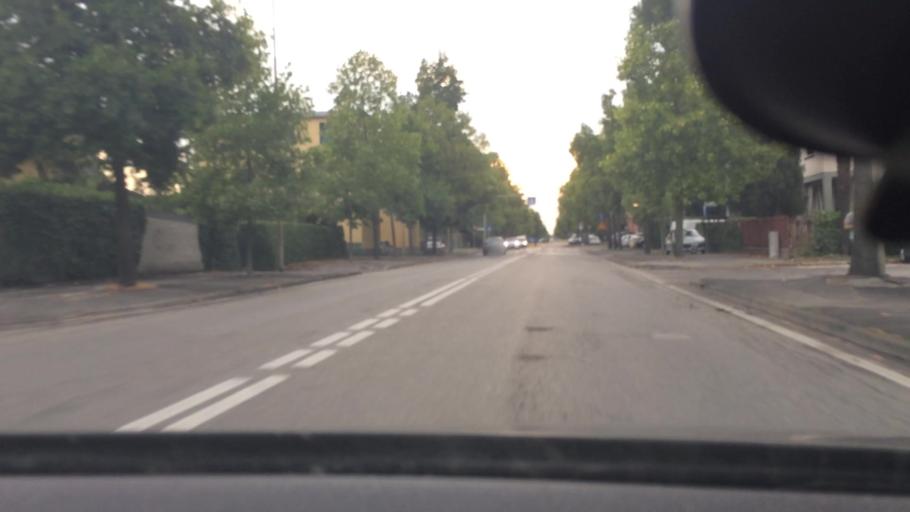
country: IT
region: Lombardy
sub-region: Provincia di Monza e Brianza
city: Nova Milanese
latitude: 45.5925
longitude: 9.1954
